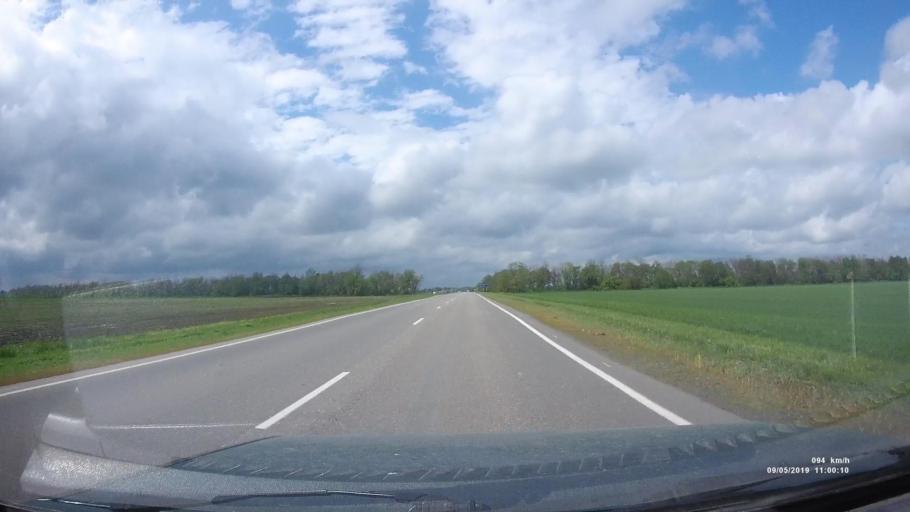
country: RU
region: Rostov
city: Peshkovo
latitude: 46.8546
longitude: 39.2258
